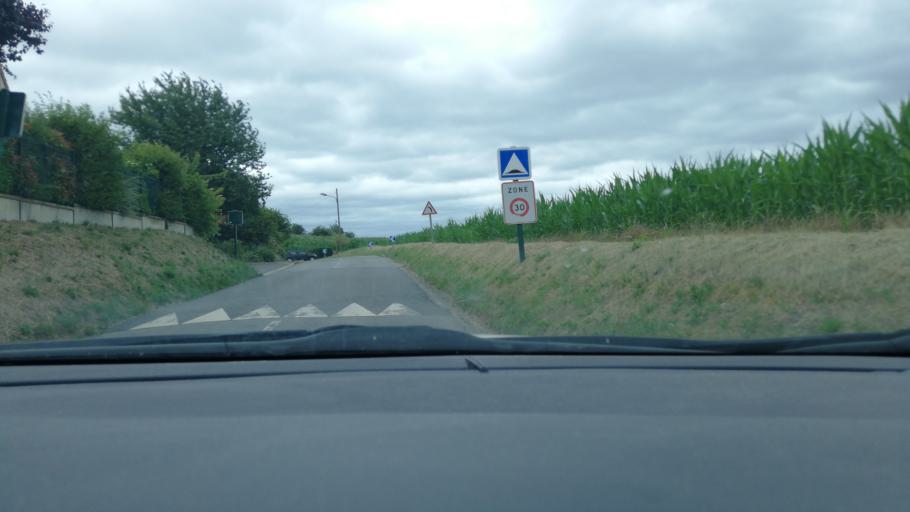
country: FR
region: Ile-de-France
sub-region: Departement du Val-d'Oise
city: Ennery
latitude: 49.0938
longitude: 2.0919
